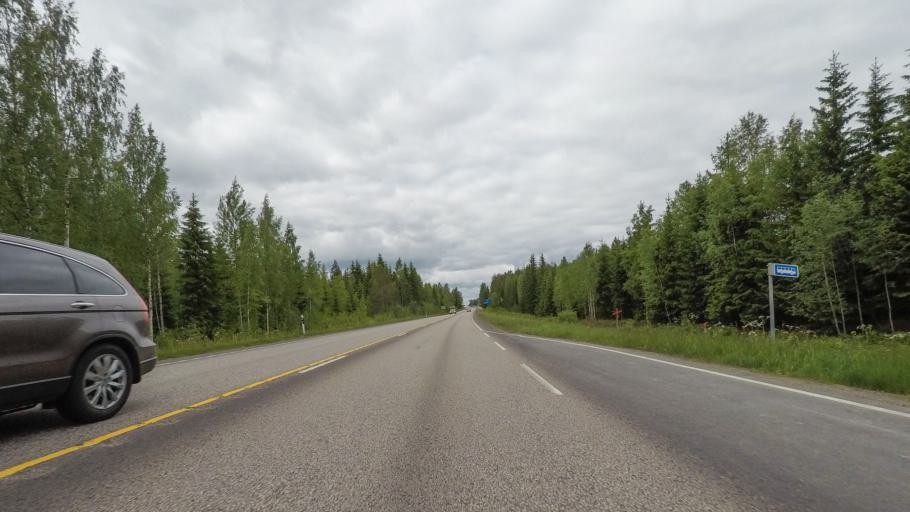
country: FI
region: Central Finland
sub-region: Joutsa
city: Joutsa
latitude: 61.7814
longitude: 26.0958
